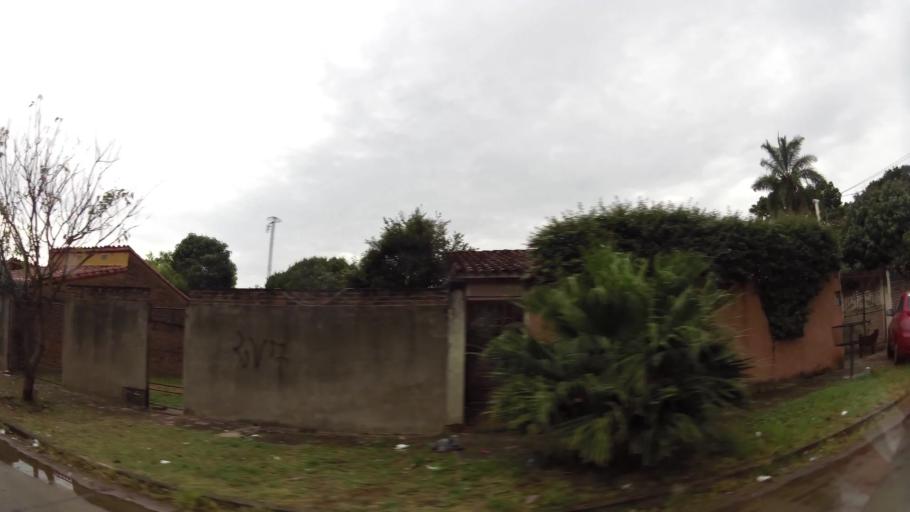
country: BO
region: Santa Cruz
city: Santa Cruz de la Sierra
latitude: -17.7812
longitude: -63.1355
